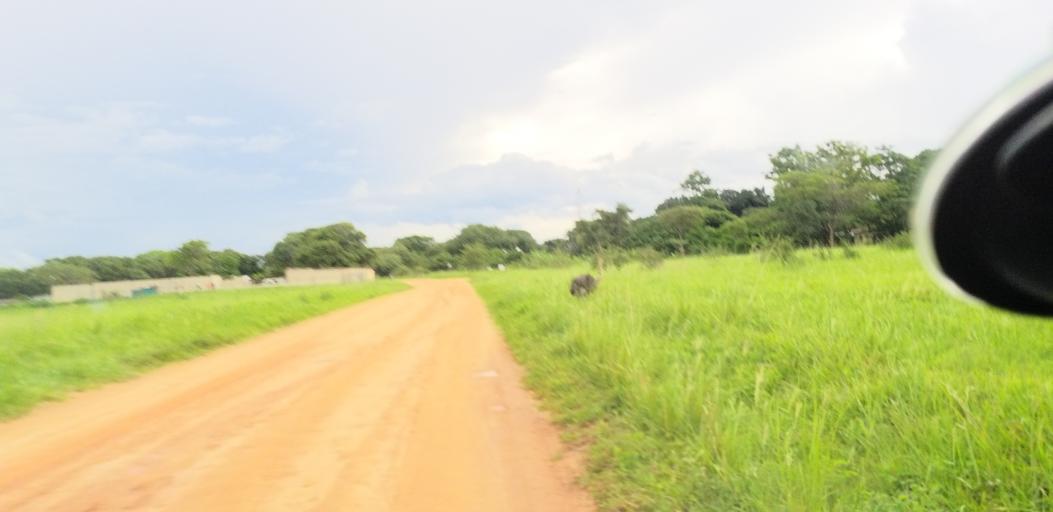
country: ZM
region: Lusaka
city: Chongwe
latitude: -15.1586
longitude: 28.4863
